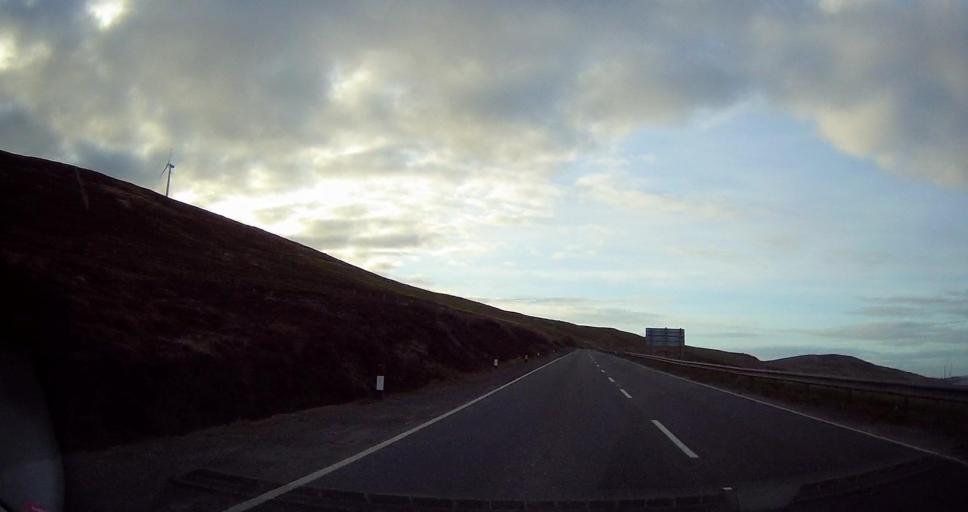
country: GB
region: Scotland
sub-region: Shetland Islands
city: Lerwick
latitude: 60.1614
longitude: -1.2267
